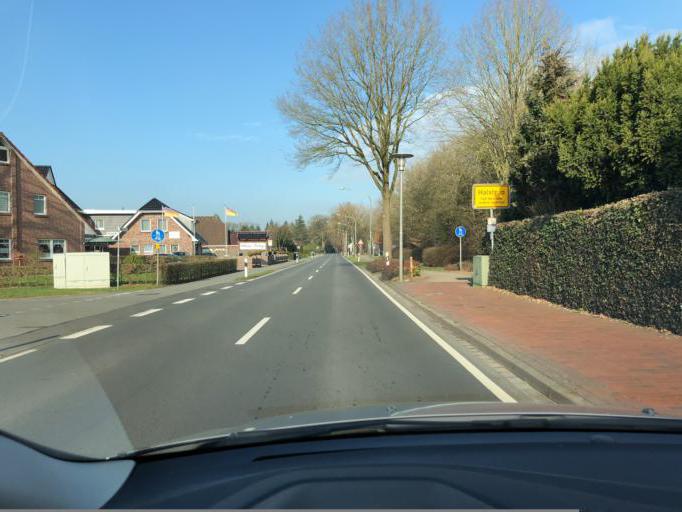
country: DE
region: Lower Saxony
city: Westerstede
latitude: 53.2611
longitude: 7.9169
